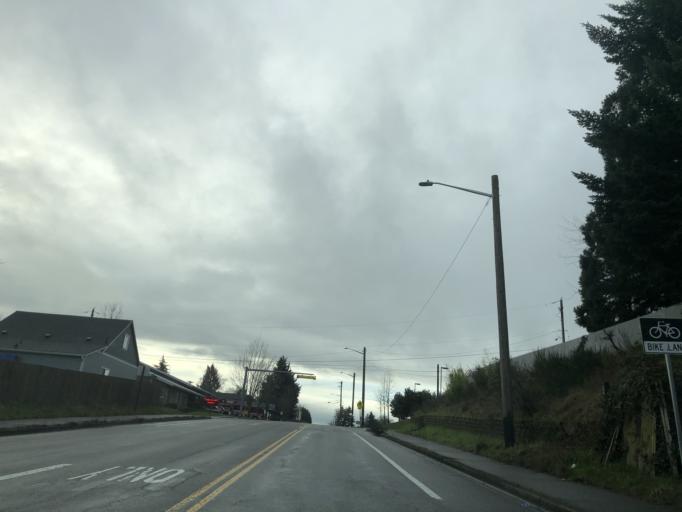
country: US
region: Washington
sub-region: Pierce County
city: Tacoma
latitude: 47.2137
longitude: -122.4584
